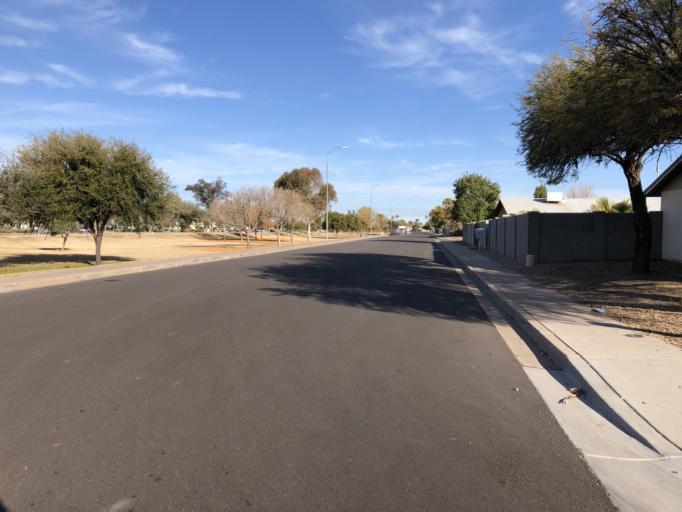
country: US
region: Arizona
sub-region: Maricopa County
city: Chandler
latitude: 33.3085
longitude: -111.9103
